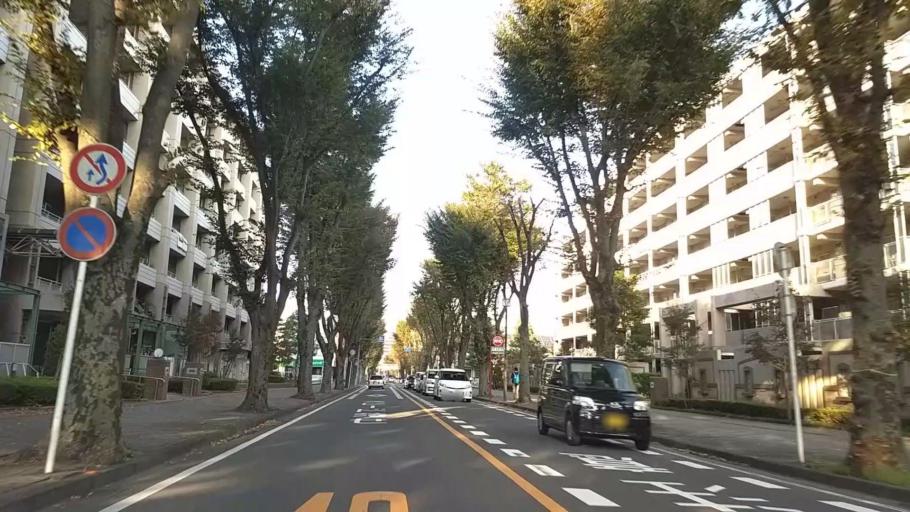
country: JP
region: Saitama
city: Tokorozawa
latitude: 35.8011
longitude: 139.4487
